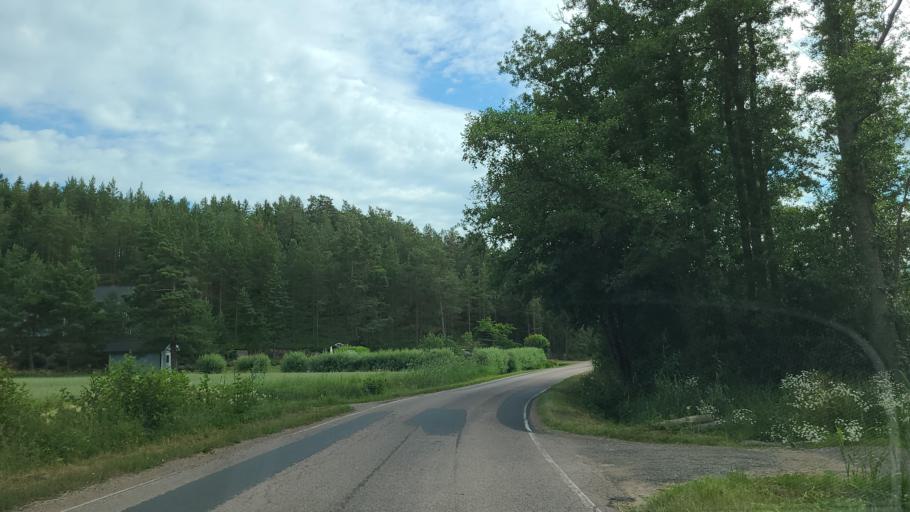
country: FI
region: Varsinais-Suomi
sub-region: Turku
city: Rymaettylae
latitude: 60.3441
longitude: 21.9785
